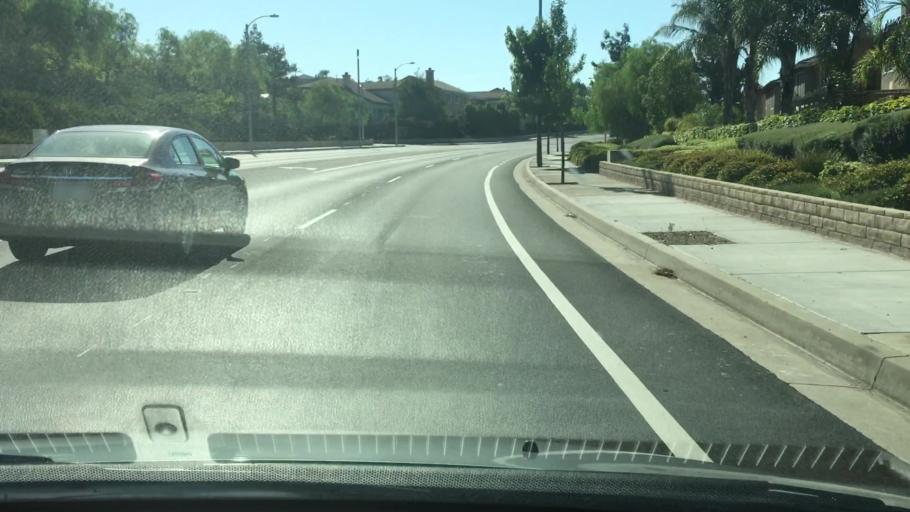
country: US
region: California
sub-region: Los Angeles County
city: Santa Clarita
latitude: 34.4607
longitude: -118.5268
